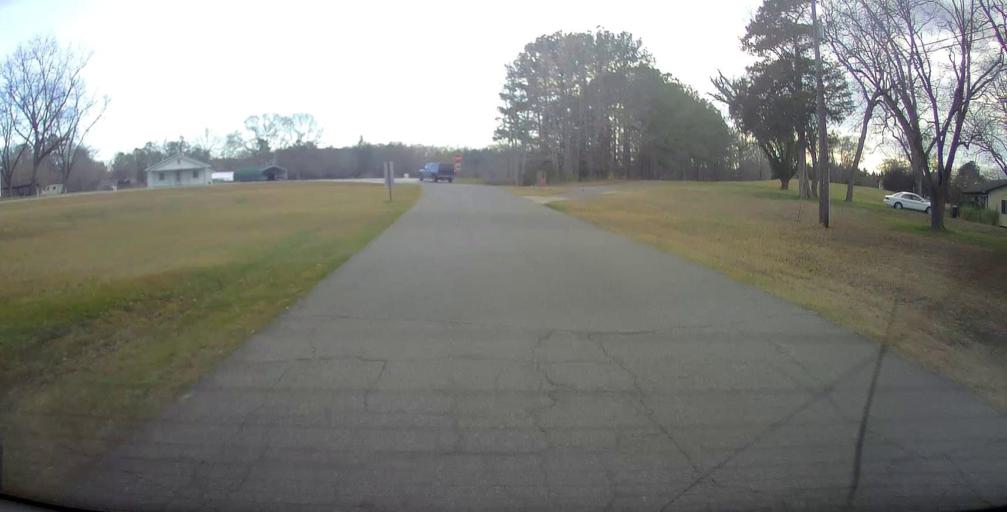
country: US
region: Georgia
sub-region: Harris County
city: Hamilton
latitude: 32.6797
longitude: -84.7439
